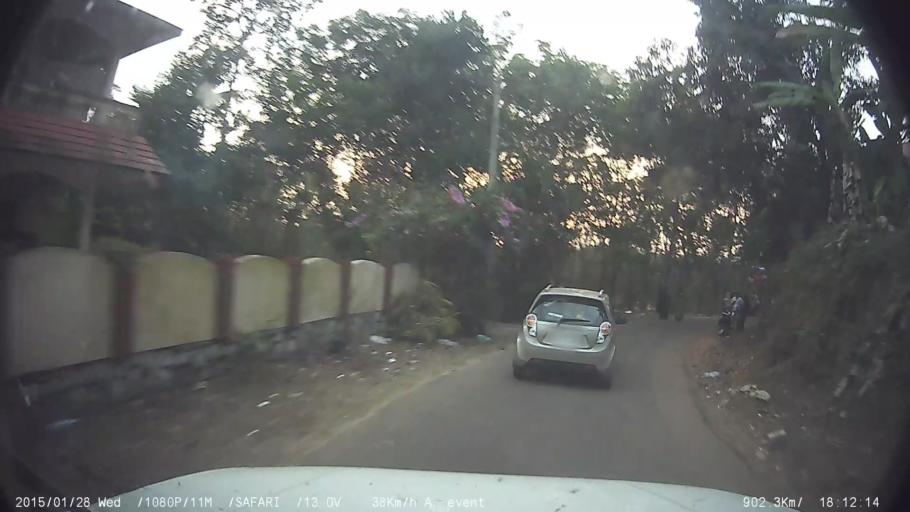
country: IN
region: Kerala
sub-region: Kottayam
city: Palackattumala
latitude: 9.7531
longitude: 76.5659
